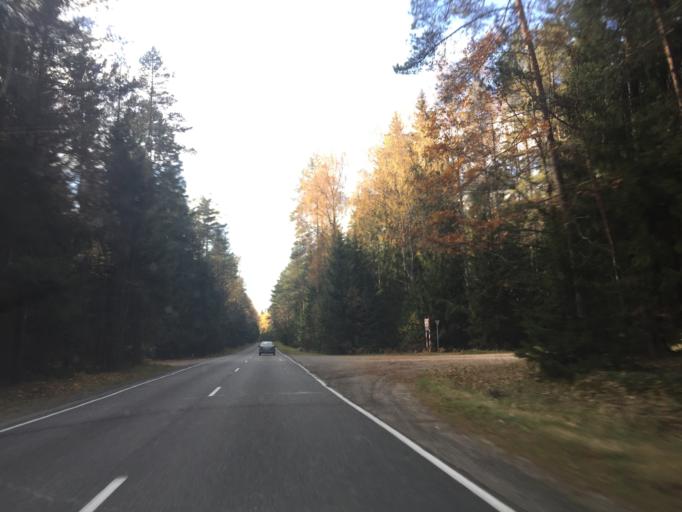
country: BY
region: Minsk
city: Narach
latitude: 54.9419
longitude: 26.5723
